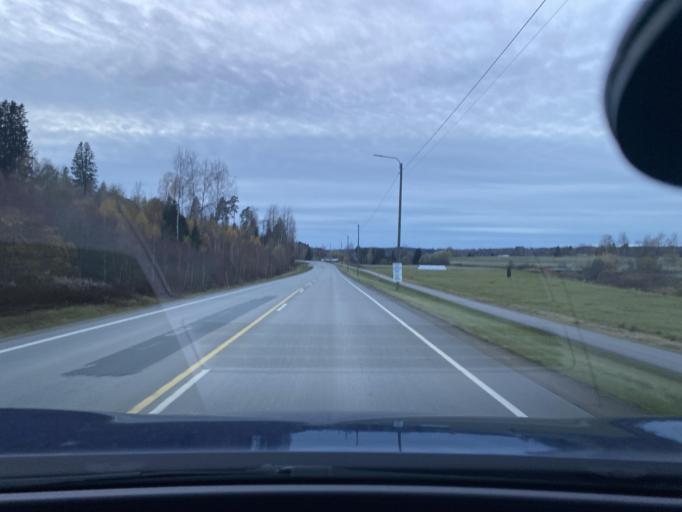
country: FI
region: Uusimaa
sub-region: Helsinki
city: Saukkola
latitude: 60.3832
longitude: 23.9402
